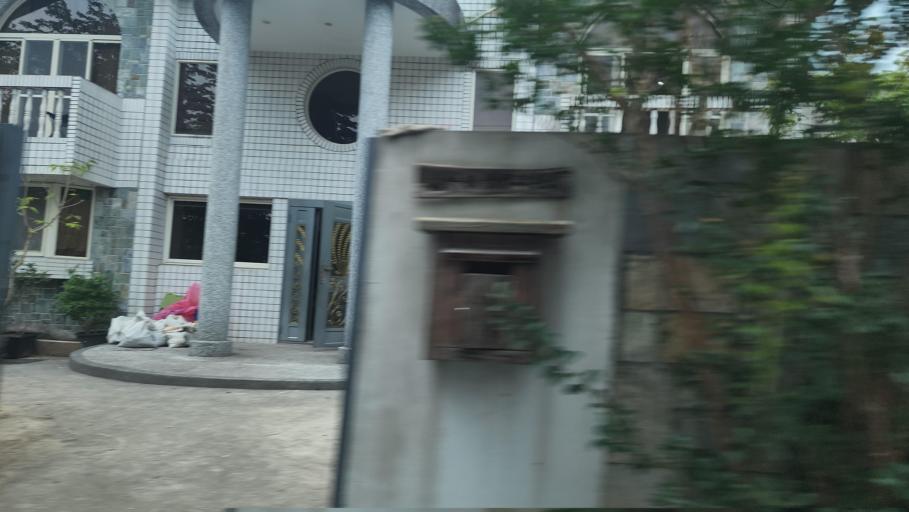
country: TW
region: Taiwan
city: Daxi
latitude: 24.9083
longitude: 121.3901
